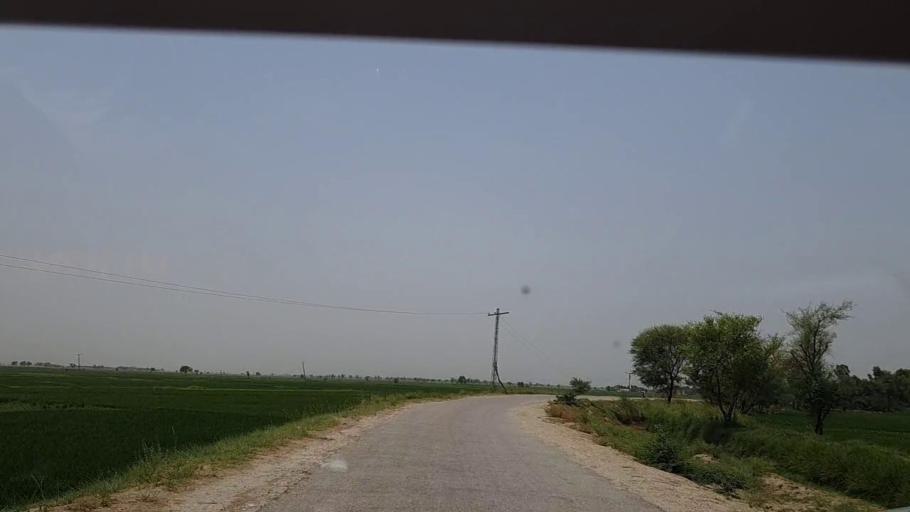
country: PK
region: Sindh
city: Khairpur Nathan Shah
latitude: 27.0087
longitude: 67.6702
